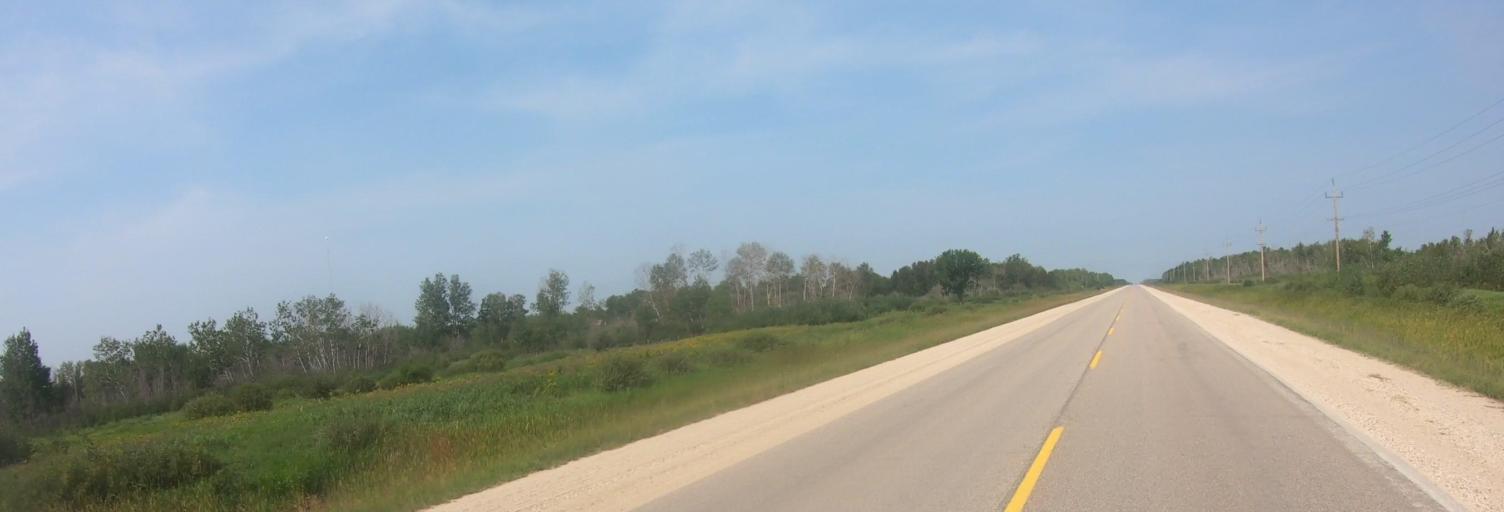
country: CA
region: Manitoba
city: La Broquerie
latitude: 49.2907
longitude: -96.5249
